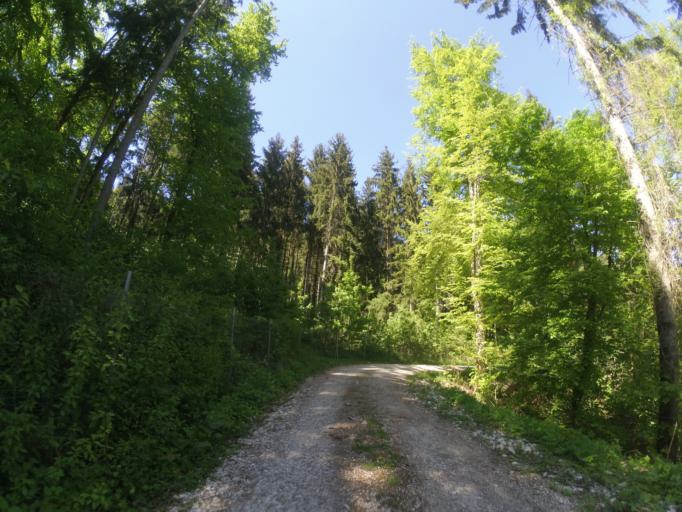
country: DE
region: Baden-Wuerttemberg
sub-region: Tuebingen Region
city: Ulm
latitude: 48.4235
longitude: 9.9665
